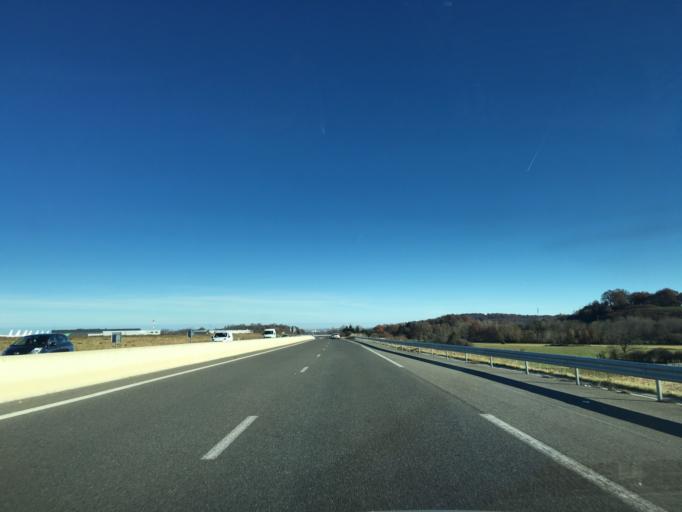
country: FR
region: Midi-Pyrenees
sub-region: Departement des Hautes-Pyrenees
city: Ossun
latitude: 43.1658
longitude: -0.0079
